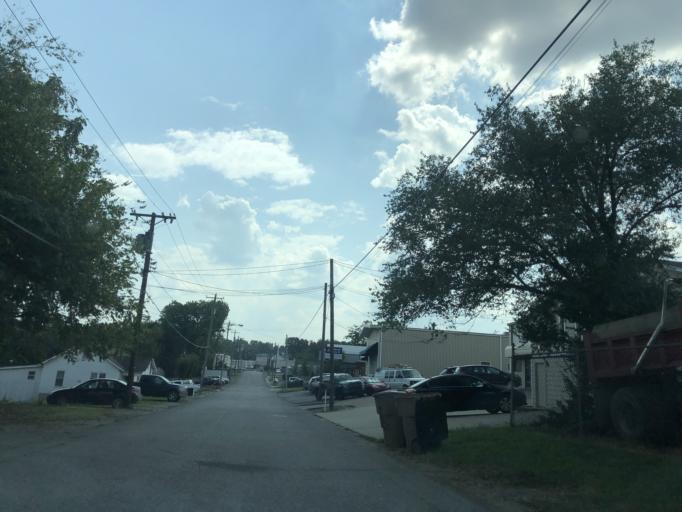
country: US
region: Tennessee
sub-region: Davidson County
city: Nashville
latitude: 36.1278
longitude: -86.7566
